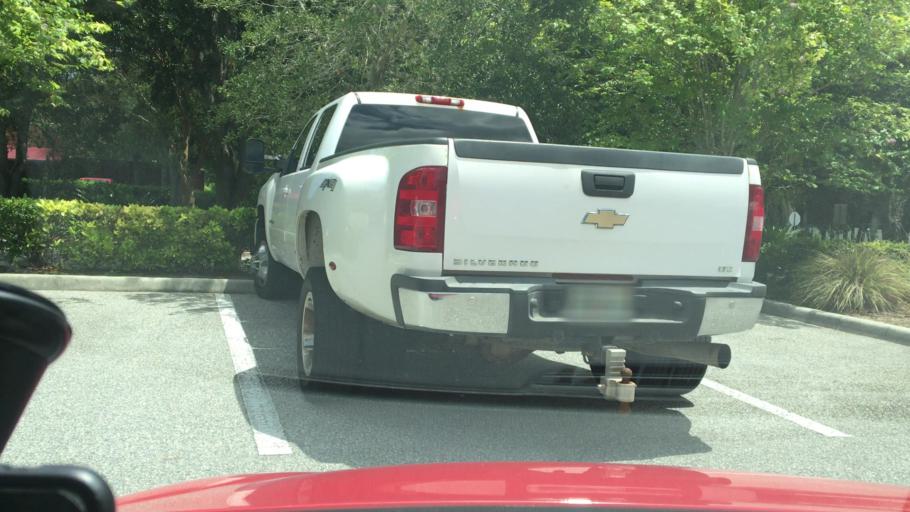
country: US
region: Florida
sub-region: Volusia County
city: Port Orange
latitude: 29.1192
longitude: -81.0174
